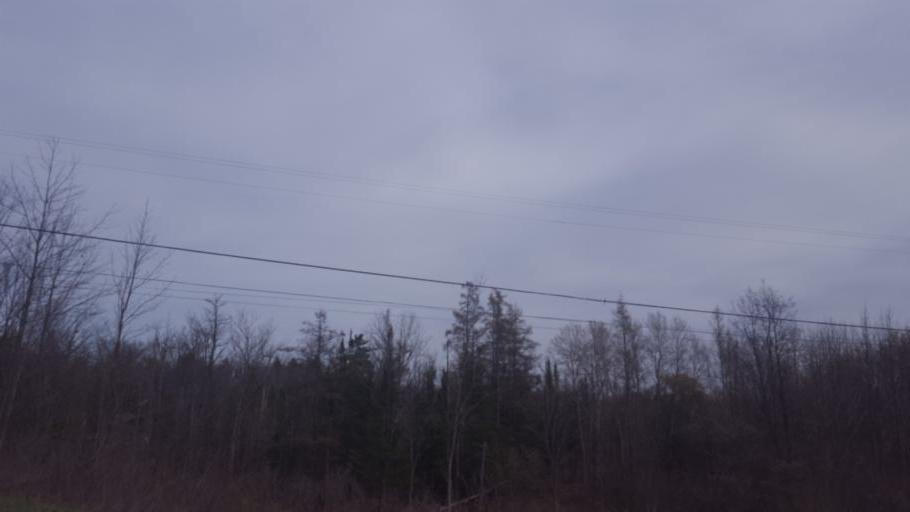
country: US
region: Michigan
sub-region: Clare County
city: Clare
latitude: 43.8542
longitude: -84.7682
